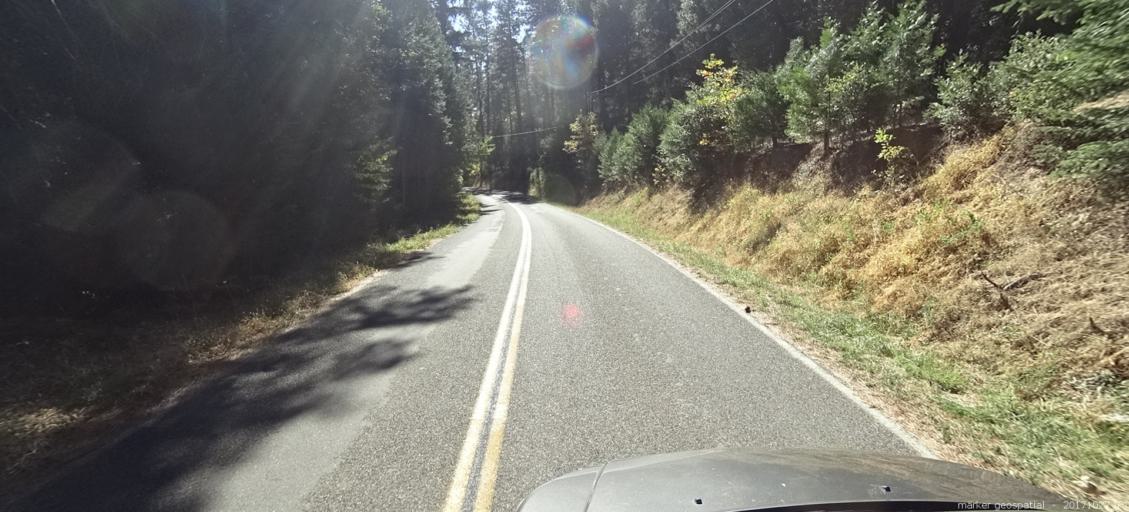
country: US
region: California
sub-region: Shasta County
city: Shingletown
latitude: 40.6918
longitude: -121.9304
